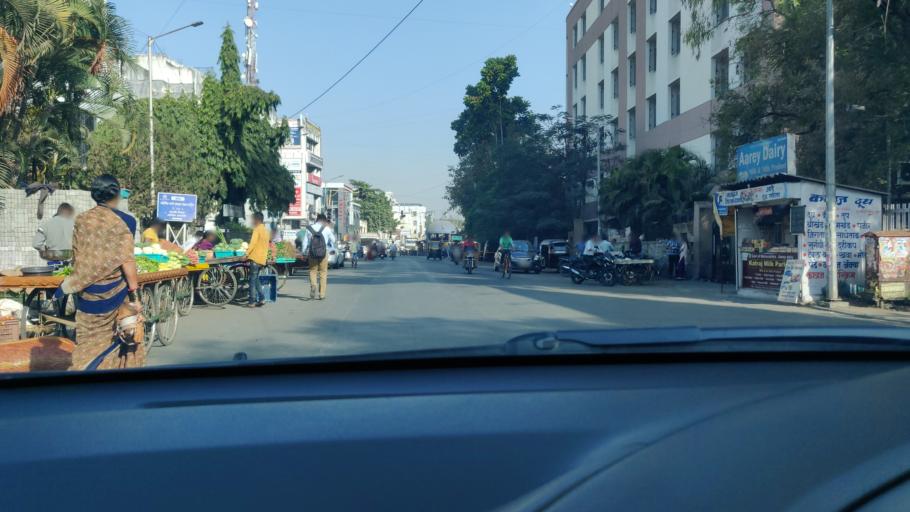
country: IN
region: Maharashtra
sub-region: Pune Division
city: Khadki
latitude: 18.5595
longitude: 73.8034
